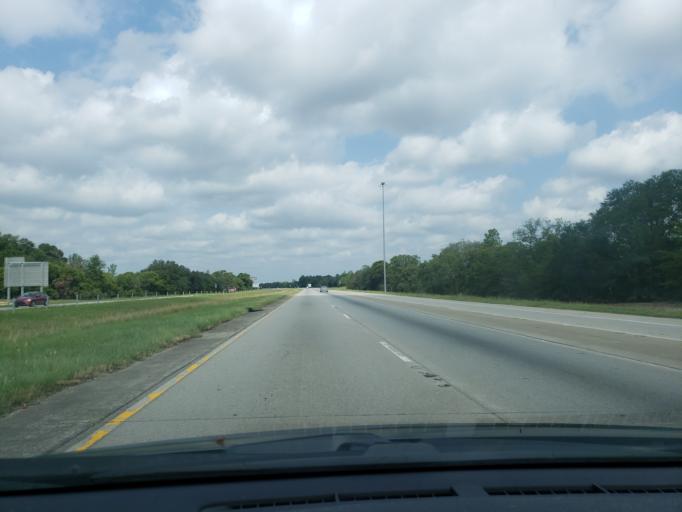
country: US
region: Georgia
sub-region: Emanuel County
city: Swainsboro
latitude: 32.4037
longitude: -82.3118
